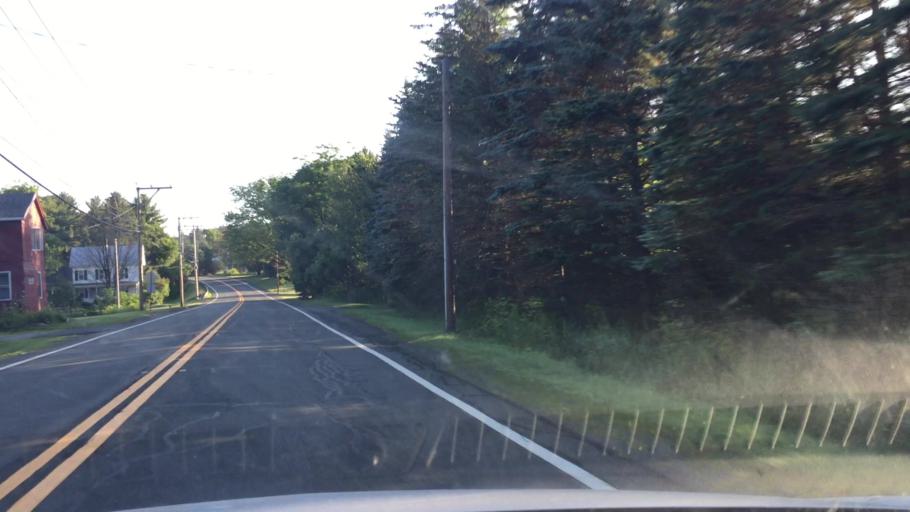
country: US
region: Massachusetts
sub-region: Berkshire County
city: Otis
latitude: 42.1978
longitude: -73.0940
